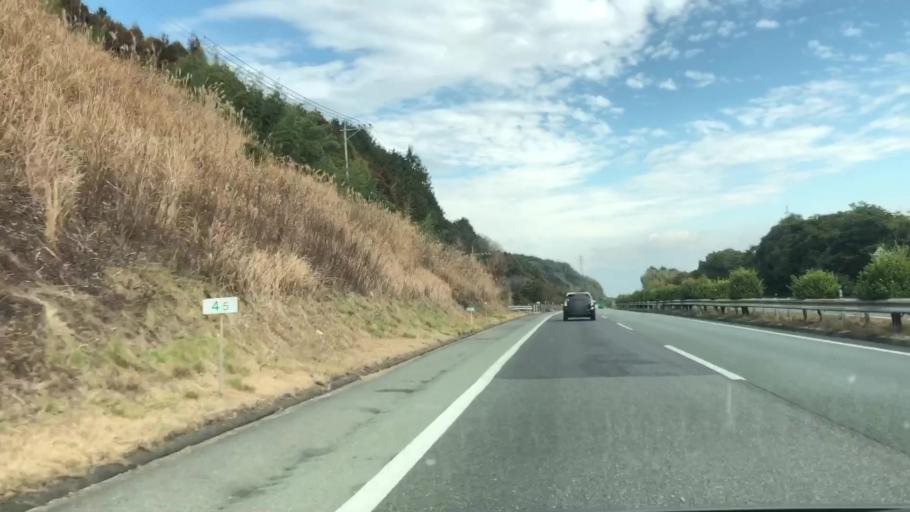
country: JP
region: Saga Prefecture
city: Tosu
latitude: 33.3921
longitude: 130.4925
